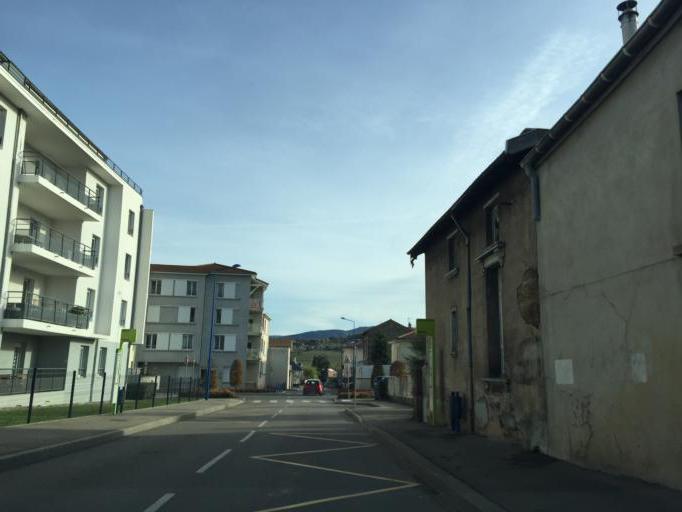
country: FR
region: Rhone-Alpes
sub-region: Departement de la Loire
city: La Talaudiere
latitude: 45.4842
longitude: 4.4366
